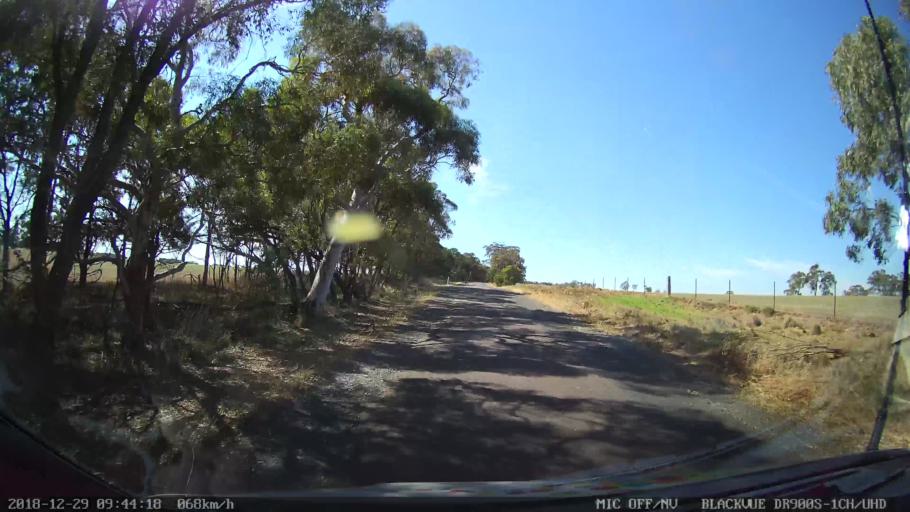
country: AU
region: New South Wales
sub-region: Upper Lachlan Shire
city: Crookwell
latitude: -34.6878
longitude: 149.4258
